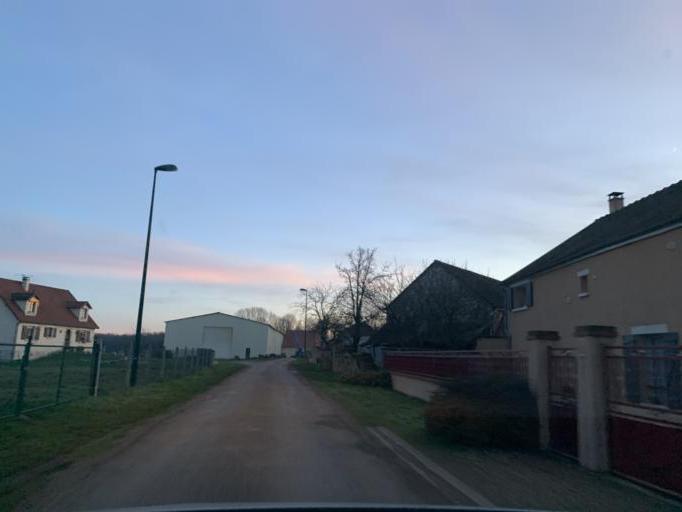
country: FR
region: Bourgogne
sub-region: Departement de l'Yonne
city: Fontenailles
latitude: 47.5627
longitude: 3.3438
